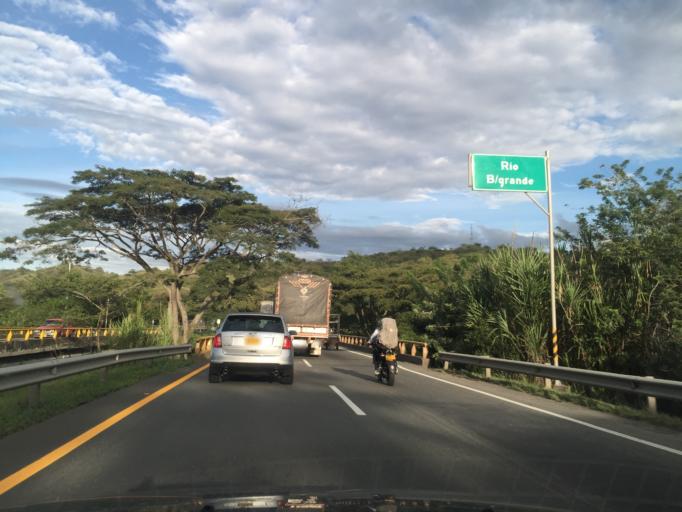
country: CO
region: Valle del Cauca
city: Bugalagrande
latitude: 4.1946
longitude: -76.1572
